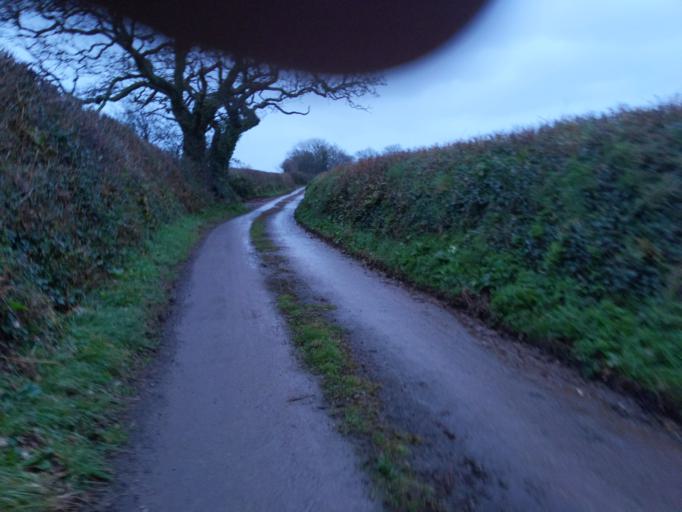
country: GB
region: England
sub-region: Devon
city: Yealmpton
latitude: 50.3323
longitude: -4.0196
